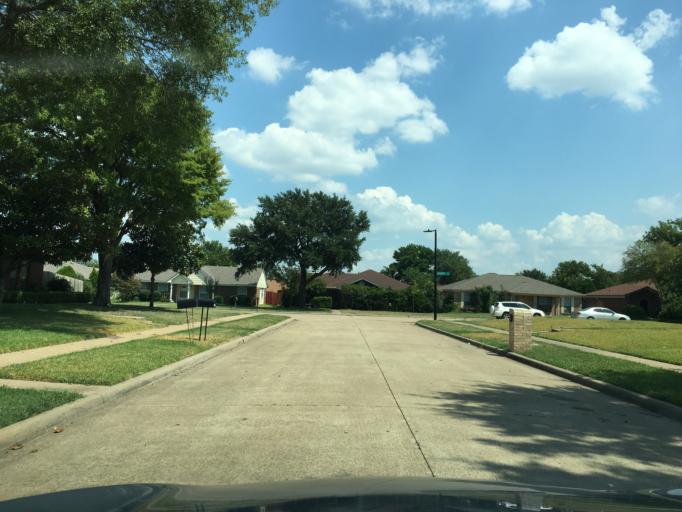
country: US
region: Texas
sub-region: Dallas County
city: Garland
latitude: 32.9510
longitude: -96.6630
